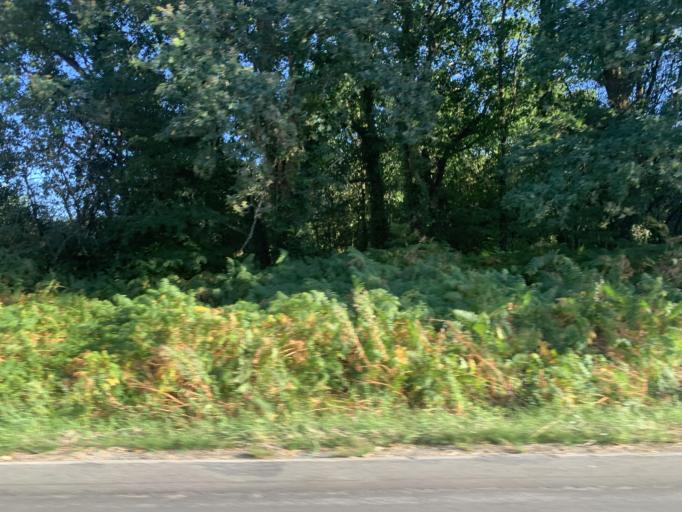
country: FR
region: Pays de la Loire
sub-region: Departement de la Loire-Atlantique
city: Pornichet
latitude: 47.2591
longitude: -2.2965
